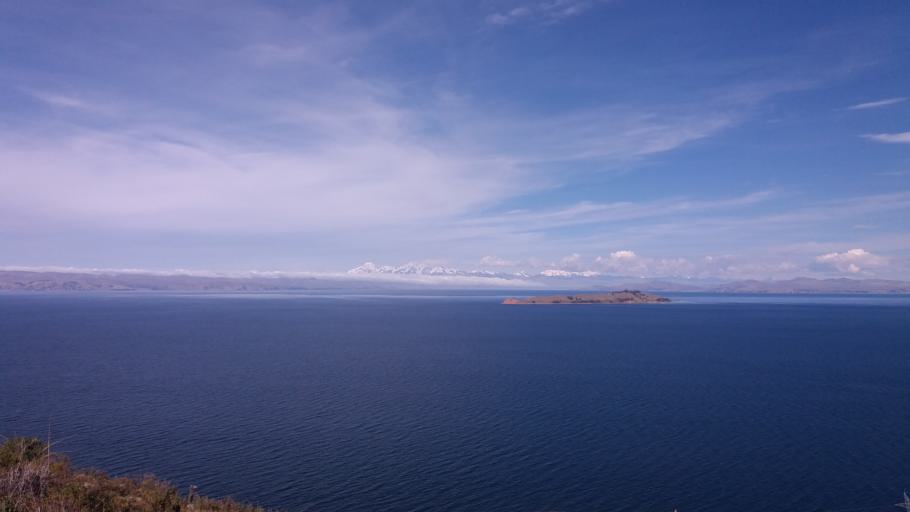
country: BO
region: La Paz
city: Yumani
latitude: -16.0433
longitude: -69.1465
